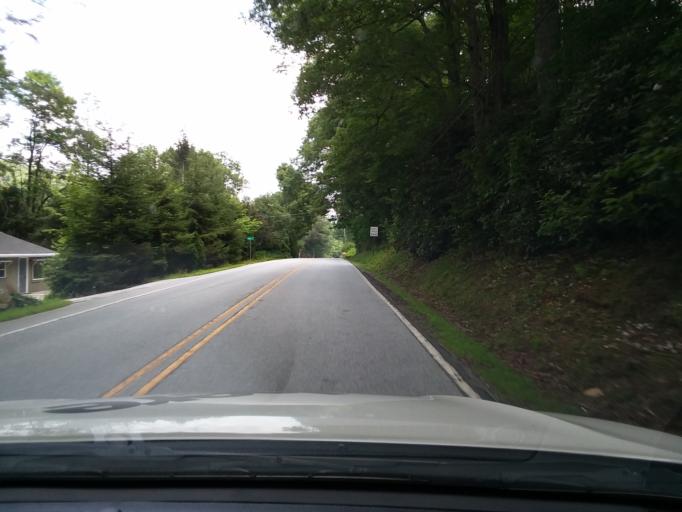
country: US
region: Georgia
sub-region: Rabun County
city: Mountain City
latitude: 35.0437
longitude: -83.2336
